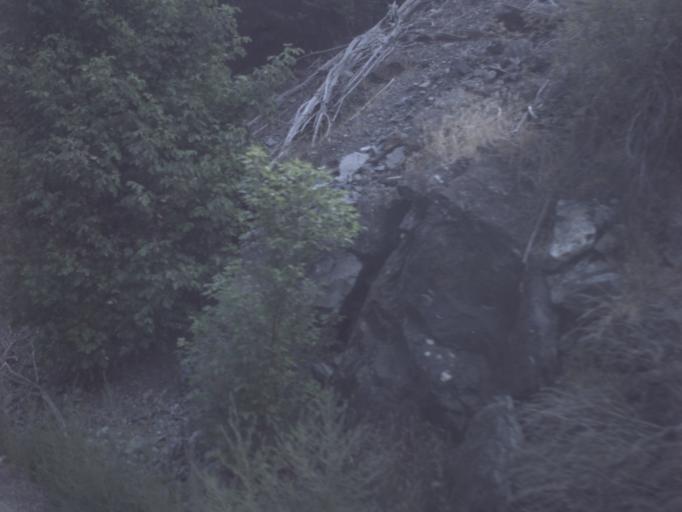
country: US
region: Utah
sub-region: Utah County
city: Cedar Hills
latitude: 40.4367
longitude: -111.7266
